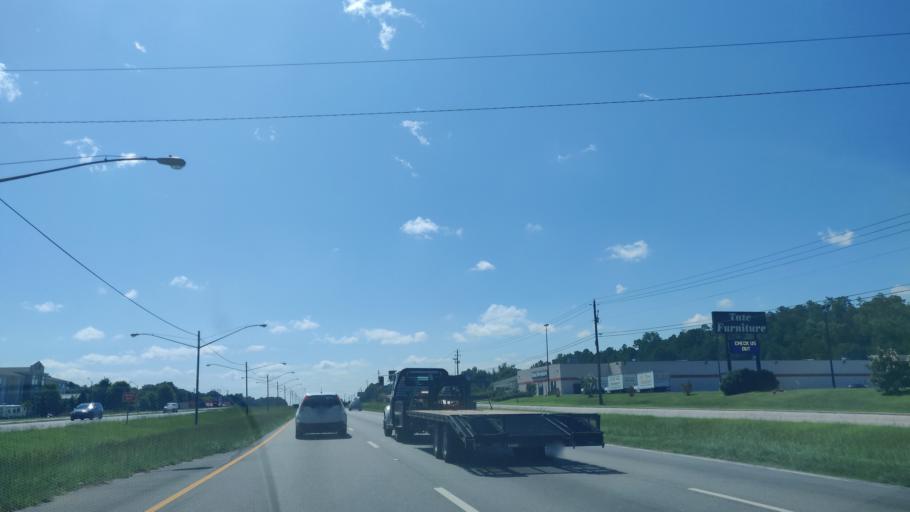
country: US
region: Alabama
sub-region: Russell County
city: Phenix City
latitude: 32.4621
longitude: -85.0215
